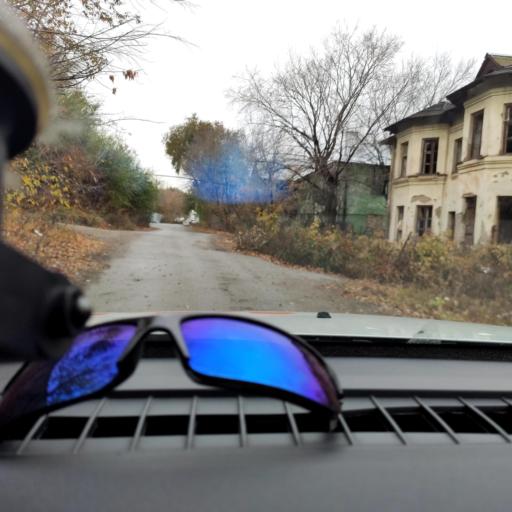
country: RU
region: Samara
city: Samara
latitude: 53.1719
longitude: 50.1738
